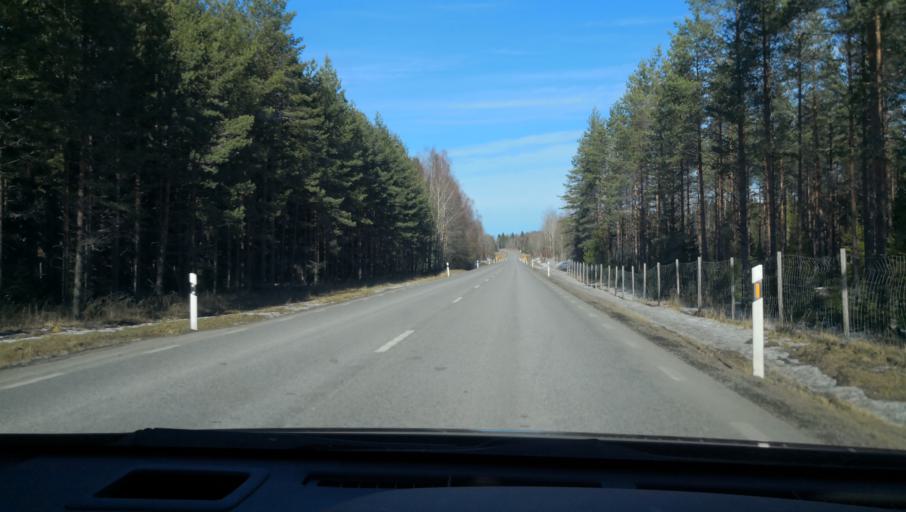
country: SE
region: Uppsala
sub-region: Uppsala Kommun
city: Vattholma
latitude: 60.0561
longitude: 17.7532
